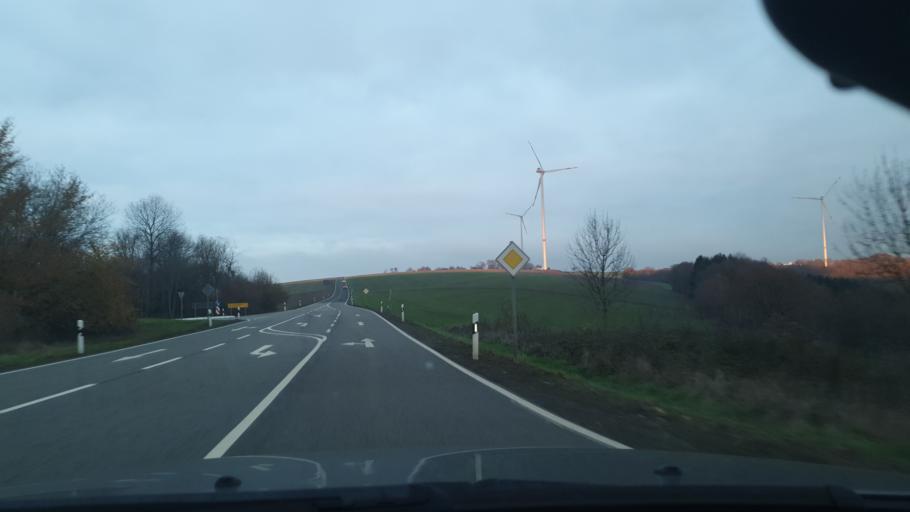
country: DE
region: Rheinland-Pfalz
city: Langwieden
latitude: 49.3680
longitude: 7.5052
